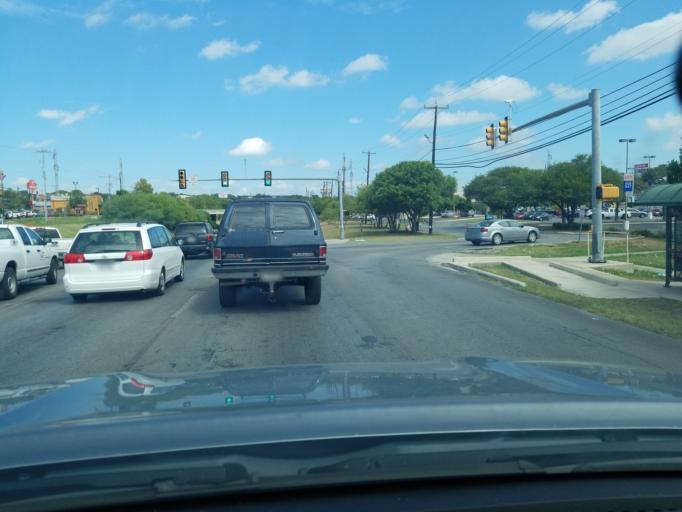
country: US
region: Texas
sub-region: Bexar County
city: Terrell Hills
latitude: 29.4920
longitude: -98.4323
